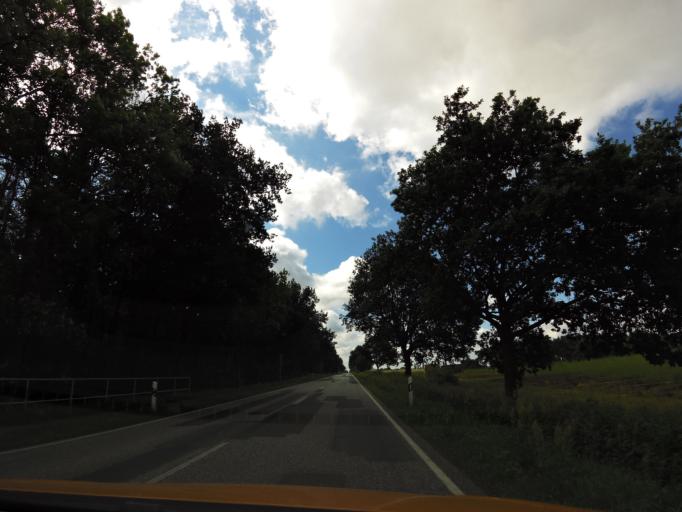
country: DE
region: Mecklenburg-Vorpommern
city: Plau am See
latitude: 53.5025
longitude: 12.2663
